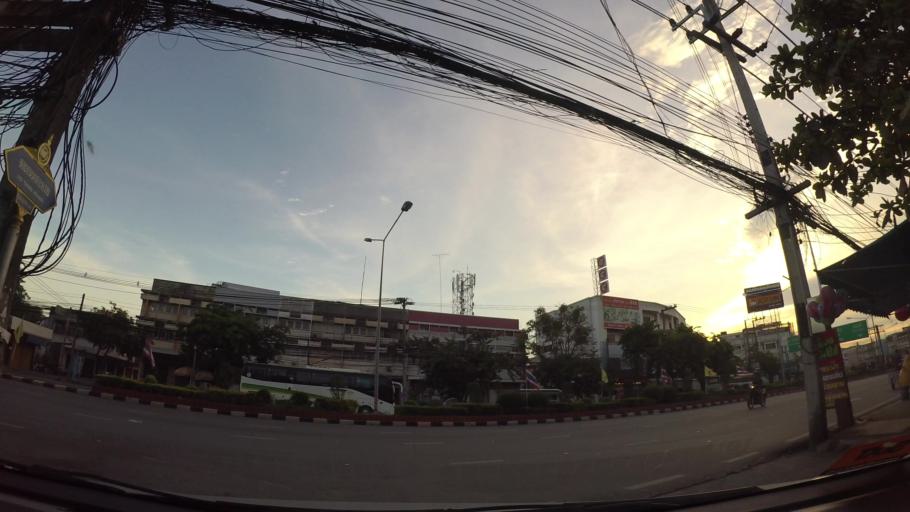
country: TH
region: Rayong
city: Rayong
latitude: 12.6805
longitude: 101.2849
